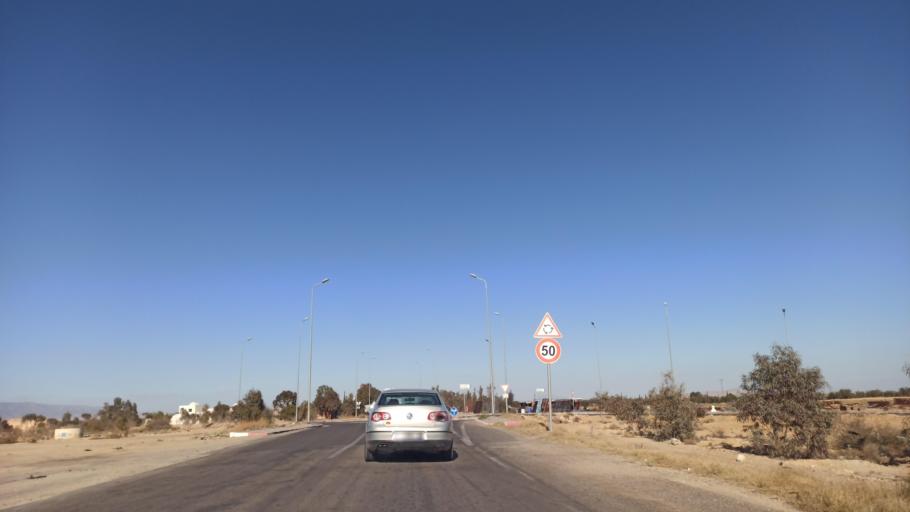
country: TN
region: Sidi Bu Zayd
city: Jilma
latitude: 35.1382
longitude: 9.3609
